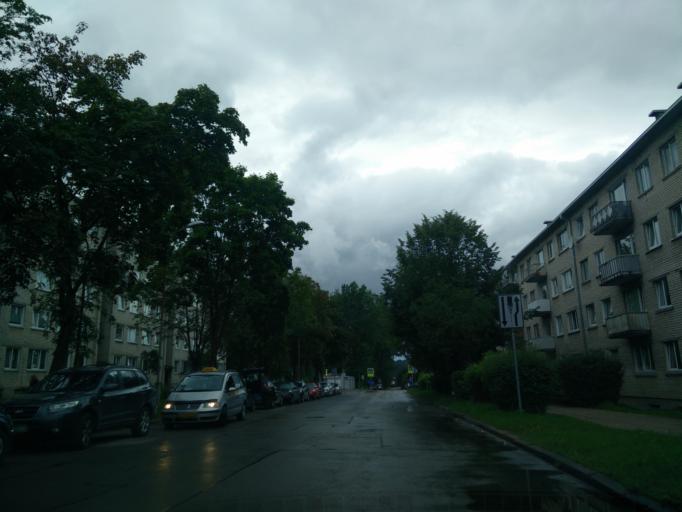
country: LT
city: Grigiskes
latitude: 54.6706
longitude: 25.0928
